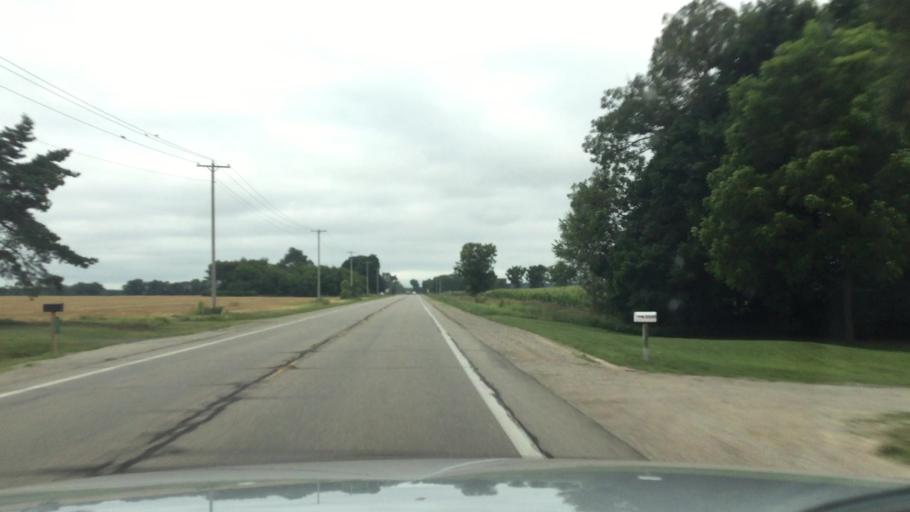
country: US
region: Michigan
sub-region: Montcalm County
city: Greenville
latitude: 43.1702
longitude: -85.1825
